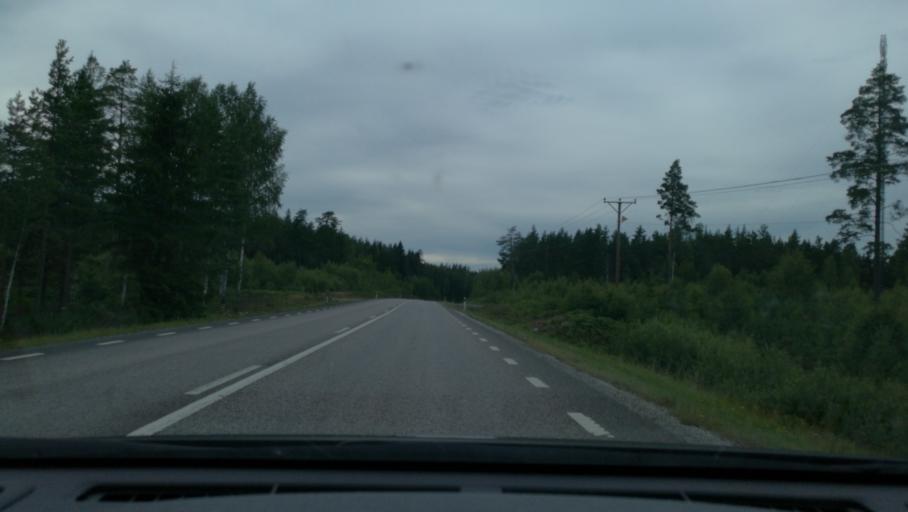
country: SE
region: Soedermanland
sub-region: Katrineholms Kommun
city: Katrineholm
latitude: 59.0832
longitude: 16.2024
